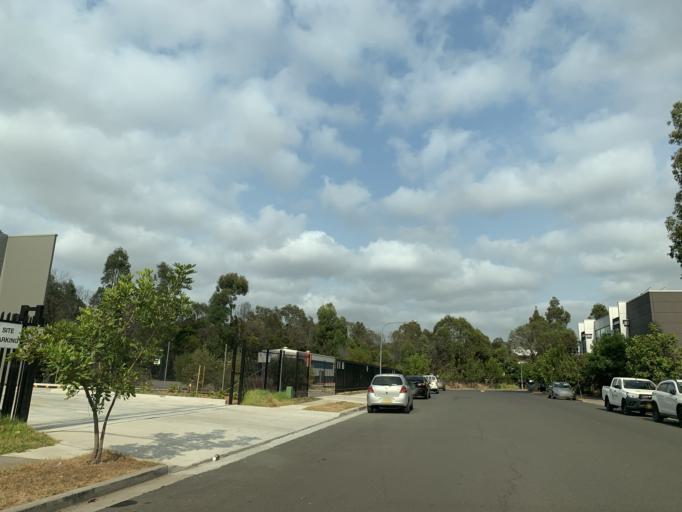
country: AU
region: New South Wales
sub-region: Holroyd
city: Girraween
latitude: -33.7767
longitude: 150.9485
